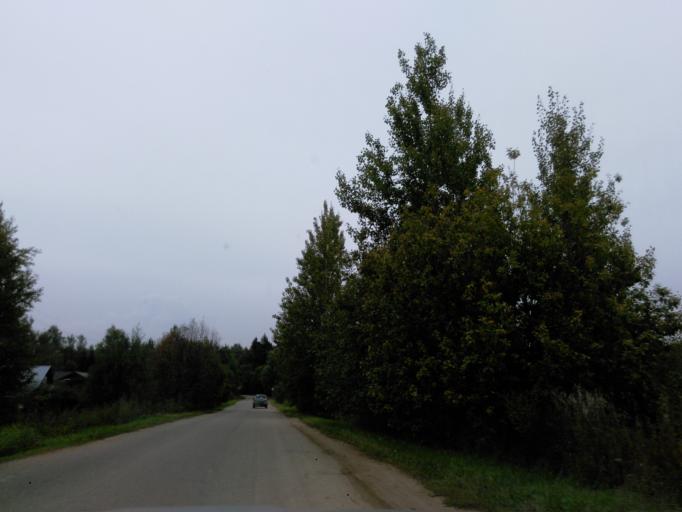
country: RU
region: Moskovskaya
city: Mendeleyevo
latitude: 56.1007
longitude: 37.2702
